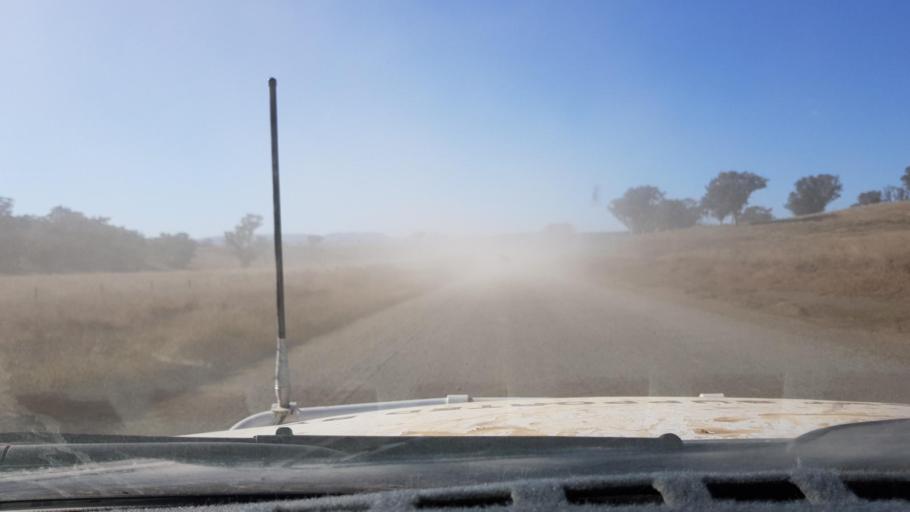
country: AU
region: New South Wales
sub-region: Narrabri
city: Blair Athol
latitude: -30.6750
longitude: 150.4160
